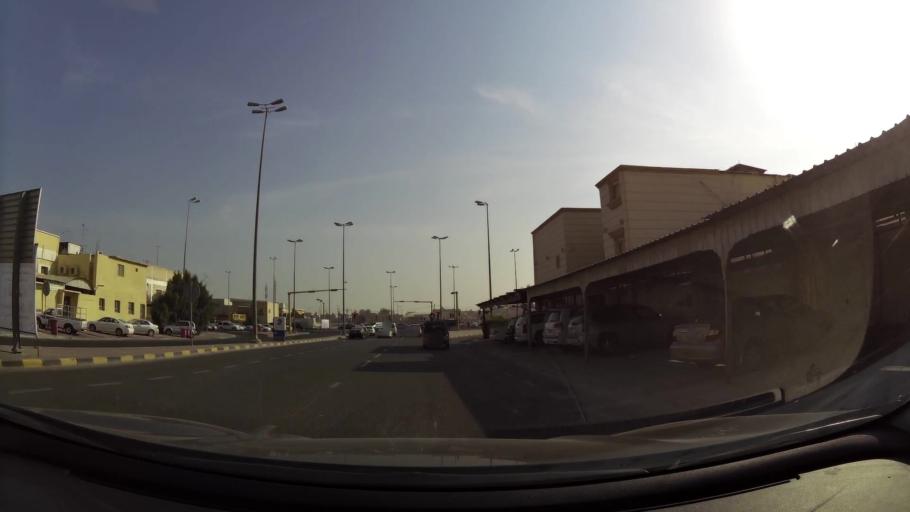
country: KW
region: Al Ahmadi
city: Ar Riqqah
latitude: 29.1362
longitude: 48.1089
